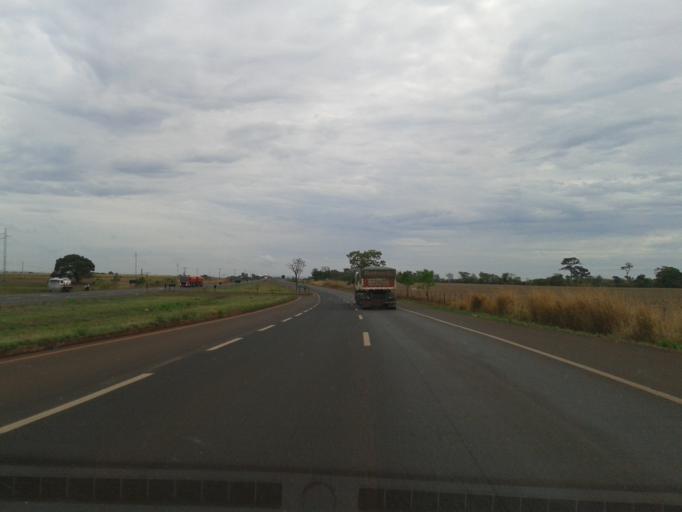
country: BR
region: Goias
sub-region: Itumbiara
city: Itumbiara
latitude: -18.4997
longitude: -49.1887
